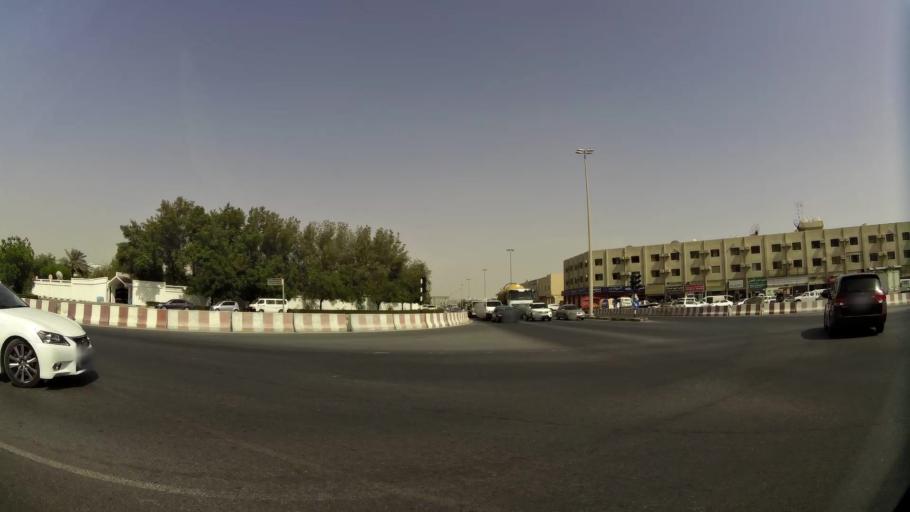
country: AE
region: Ash Shariqah
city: Sharjah
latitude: 25.3268
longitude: 55.4339
